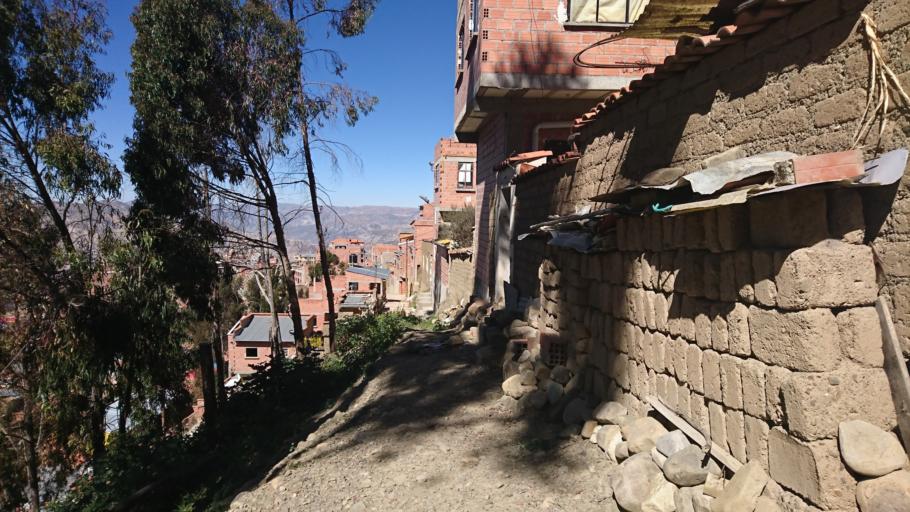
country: BO
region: La Paz
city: La Paz
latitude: -16.4899
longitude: -68.1033
